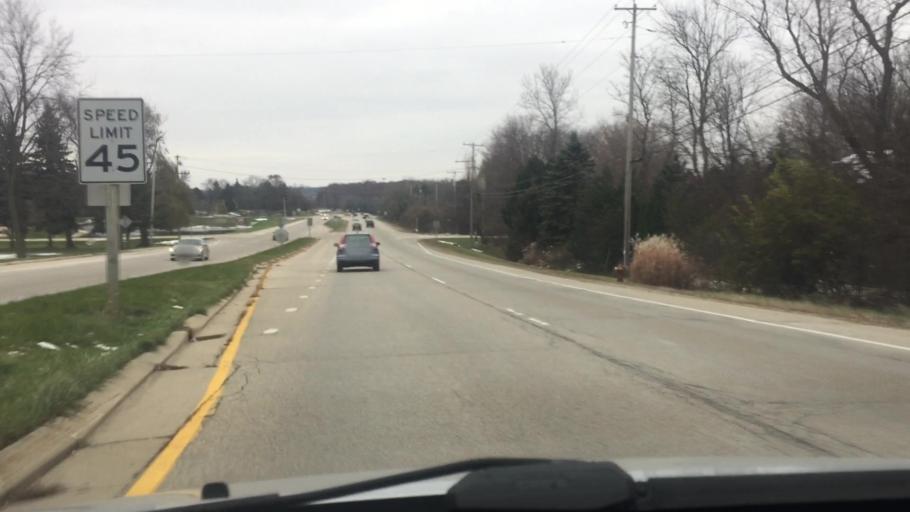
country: US
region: Wisconsin
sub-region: Waukesha County
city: Delafield
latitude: 43.0654
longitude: -88.3672
